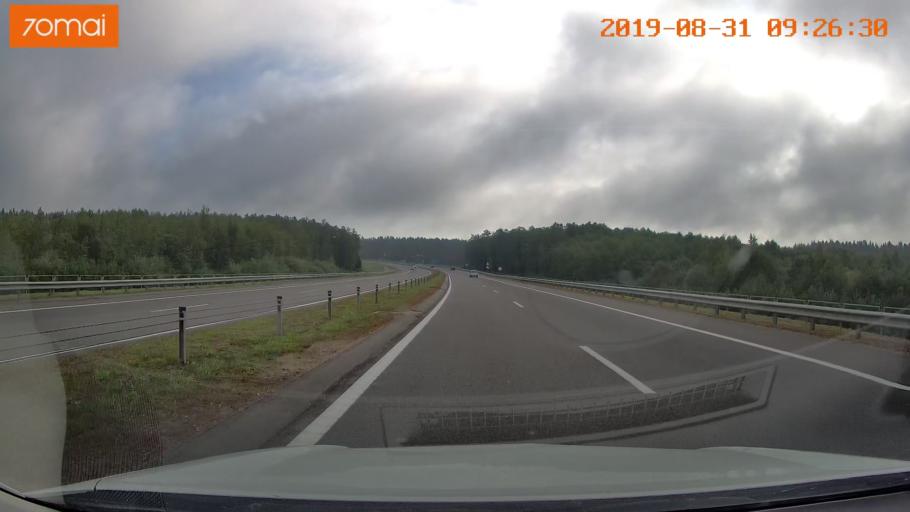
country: BY
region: Minsk
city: Byerazino
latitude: 53.8293
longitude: 29.0082
